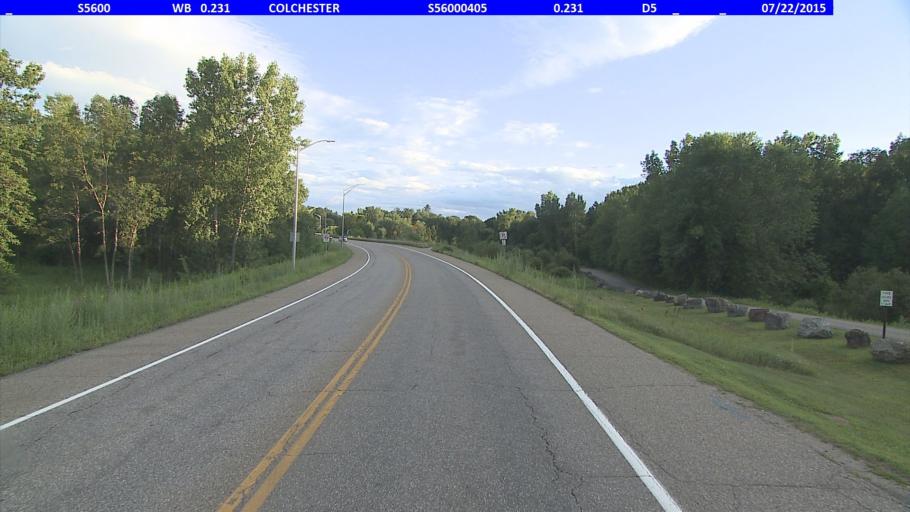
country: US
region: Vermont
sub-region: Chittenden County
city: Burlington
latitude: 44.5282
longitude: -73.2551
